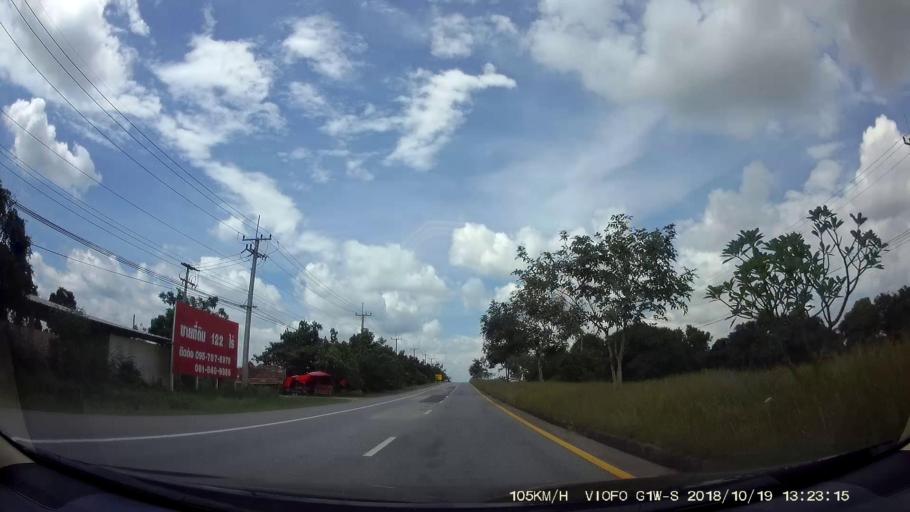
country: TH
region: Chaiyaphum
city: Chatturat
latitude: 15.4890
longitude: 101.8219
